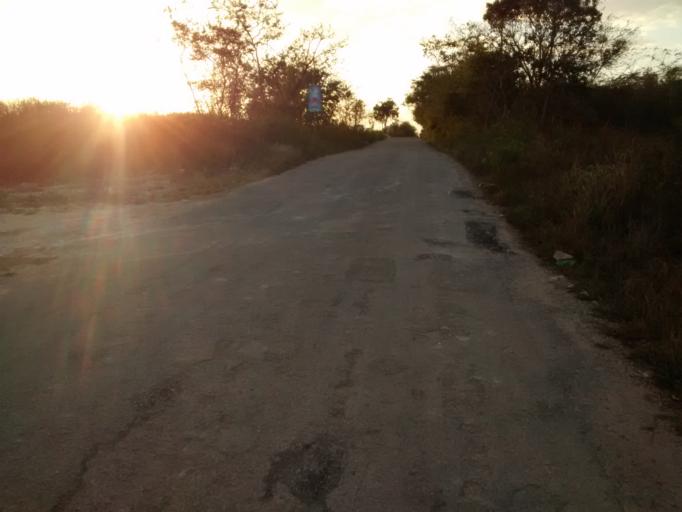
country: MX
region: Yucatan
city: Valladolid
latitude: 20.6831
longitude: -88.1724
